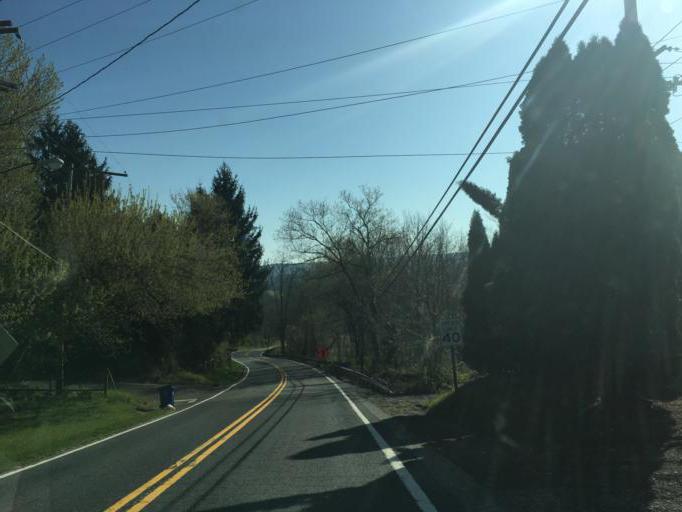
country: US
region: Maryland
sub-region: Frederick County
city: Myersville
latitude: 39.5074
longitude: -77.5656
